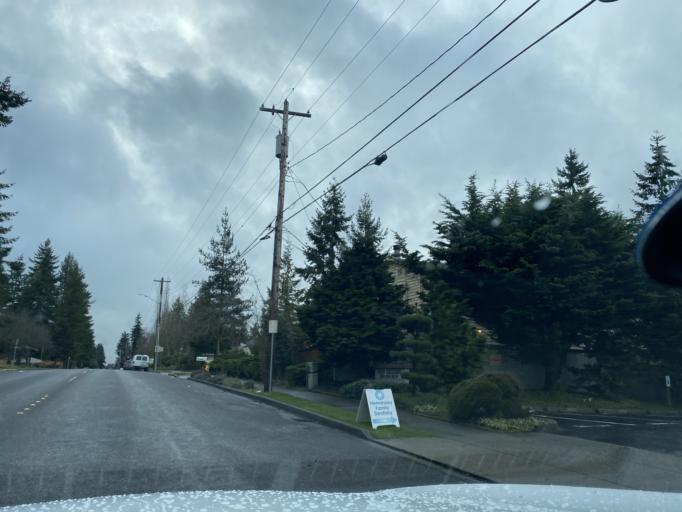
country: US
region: Washington
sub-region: Snohomish County
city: Lynnwood
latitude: 47.8333
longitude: -122.3033
